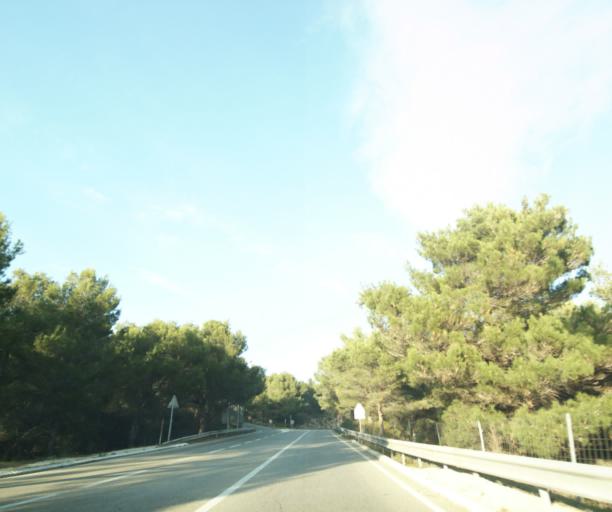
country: FR
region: Provence-Alpes-Cote d'Azur
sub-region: Departement des Bouches-du-Rhone
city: Roquefort-la-Bedoule
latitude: 43.2223
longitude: 5.5802
